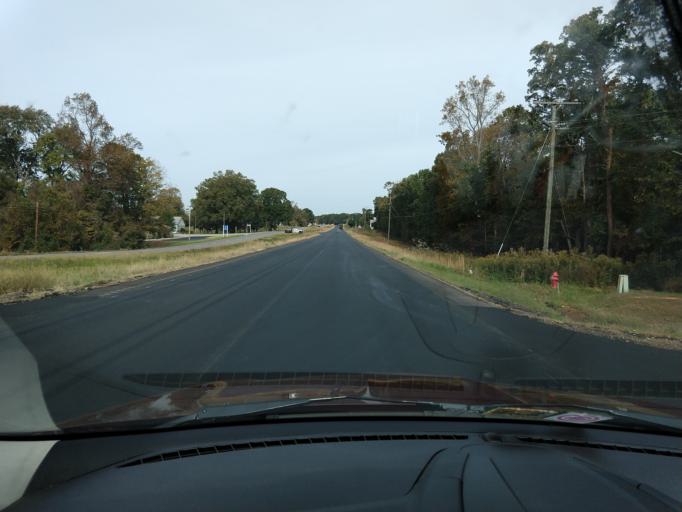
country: US
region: Virginia
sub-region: Pittsylvania County
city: Chatham
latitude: 36.8573
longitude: -79.3981
